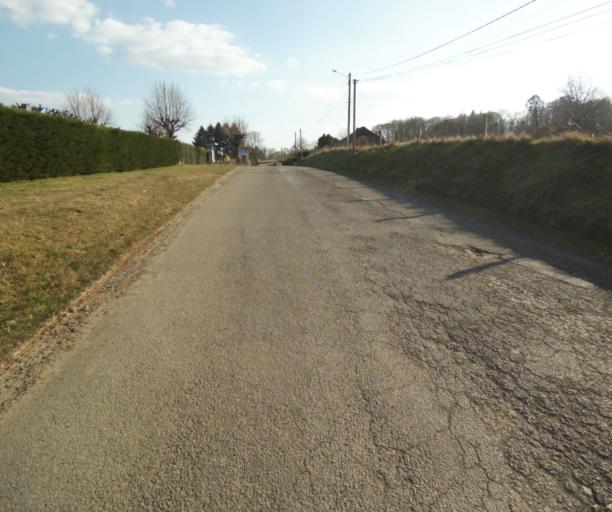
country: FR
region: Limousin
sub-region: Departement de la Correze
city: Saint-Clement
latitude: 45.3502
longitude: 1.6451
